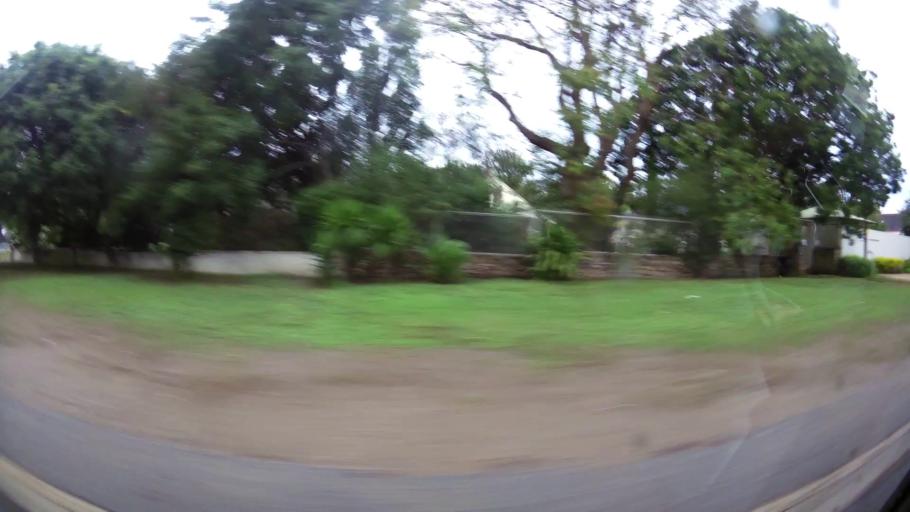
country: ZA
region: Eastern Cape
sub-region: Nelson Mandela Bay Metropolitan Municipality
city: Port Elizabeth
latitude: -33.9819
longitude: 25.5762
